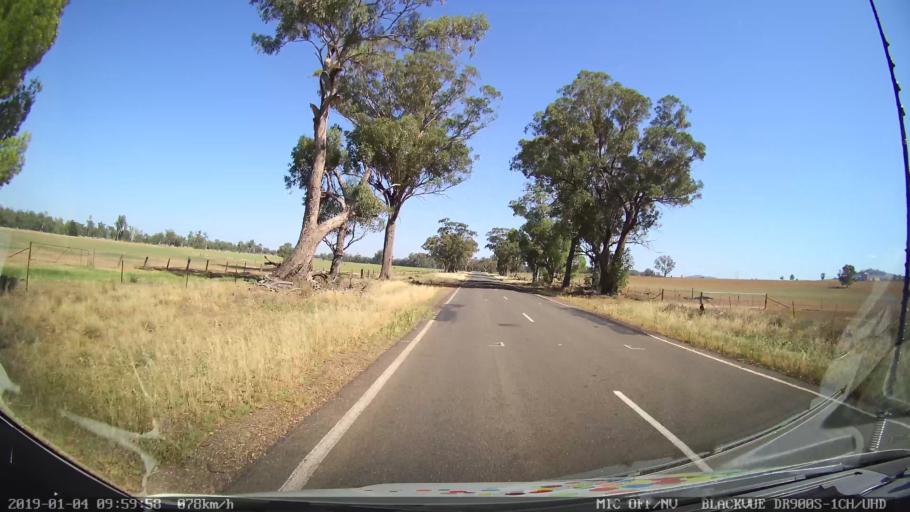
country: AU
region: New South Wales
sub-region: Cabonne
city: Canowindra
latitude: -33.5025
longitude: 148.3824
